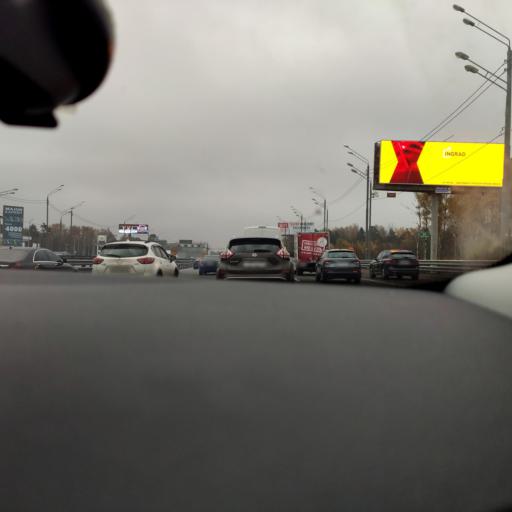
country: RU
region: Moskovskaya
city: Opalikha
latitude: 55.7886
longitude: 37.2572
